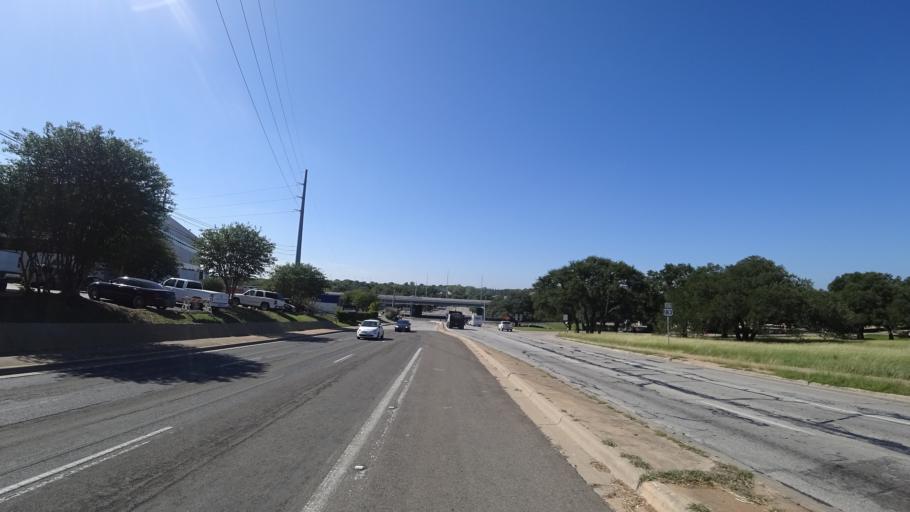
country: US
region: Texas
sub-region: Travis County
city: Austin
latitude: 30.3341
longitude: -97.6854
